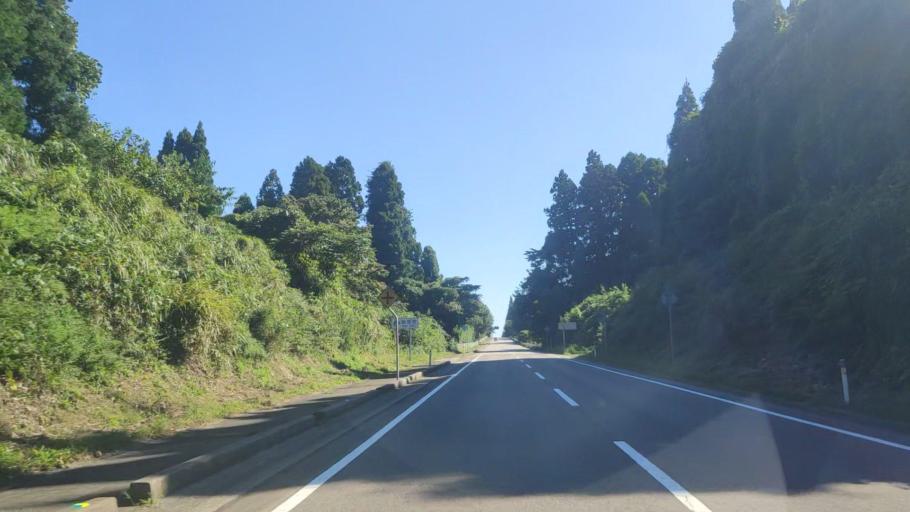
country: JP
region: Ishikawa
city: Nanao
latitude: 37.3736
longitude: 137.2348
